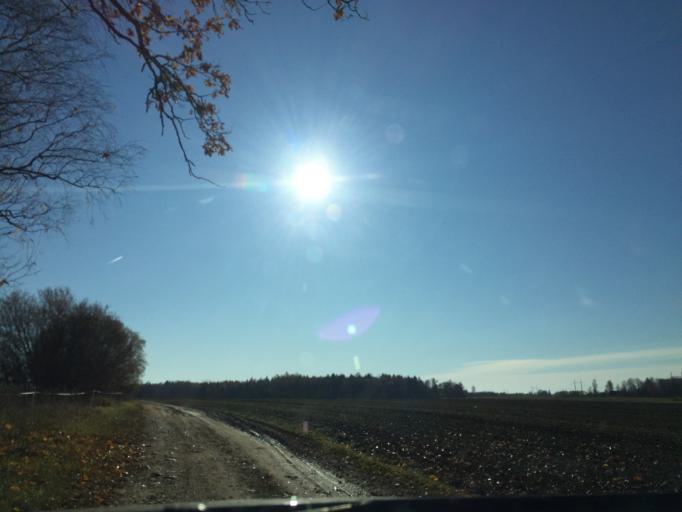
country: LV
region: Skriveri
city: Skriveri
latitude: 56.6651
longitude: 25.1728
